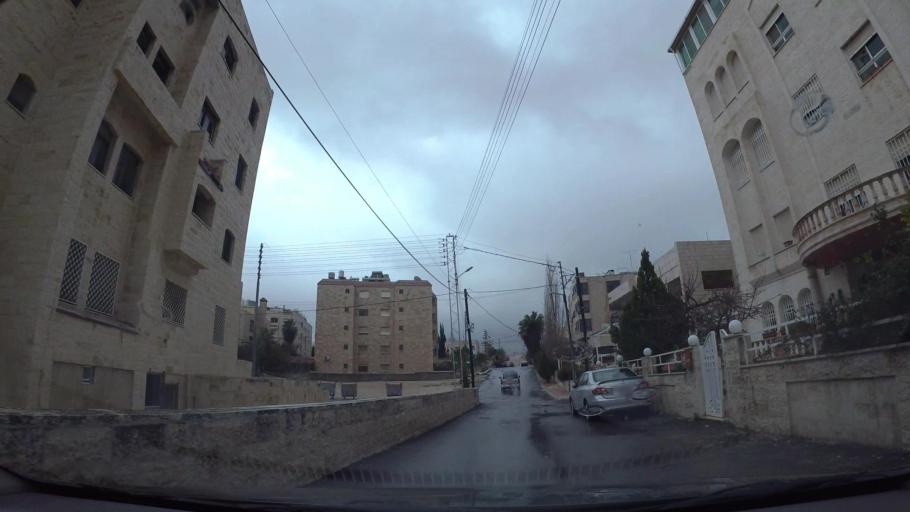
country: JO
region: Amman
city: Al Jubayhah
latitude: 32.0290
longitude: 35.8733
